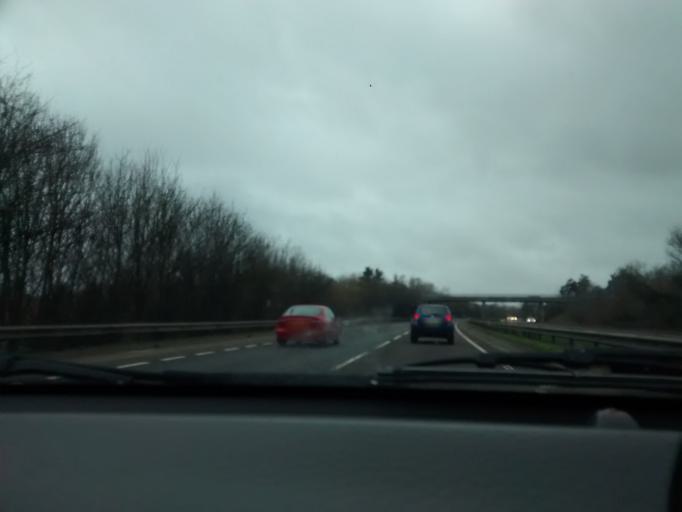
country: GB
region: England
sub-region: Suffolk
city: Bramford
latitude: 52.1157
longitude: 1.1031
